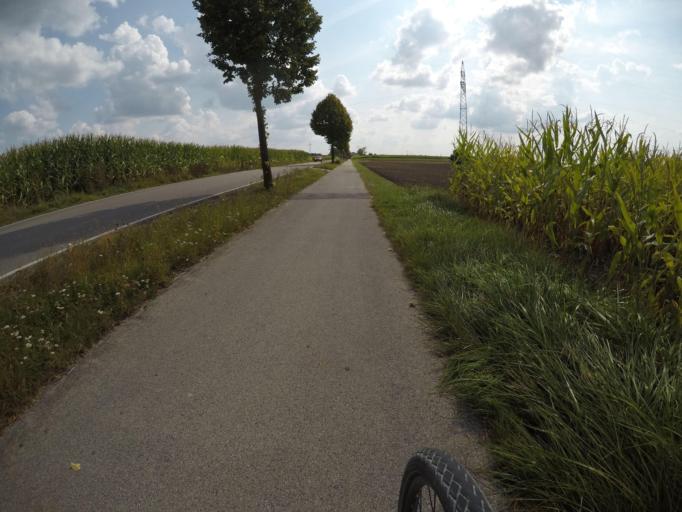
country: DE
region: Bavaria
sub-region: Swabia
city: Westendorf
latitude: 48.5586
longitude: 10.8441
